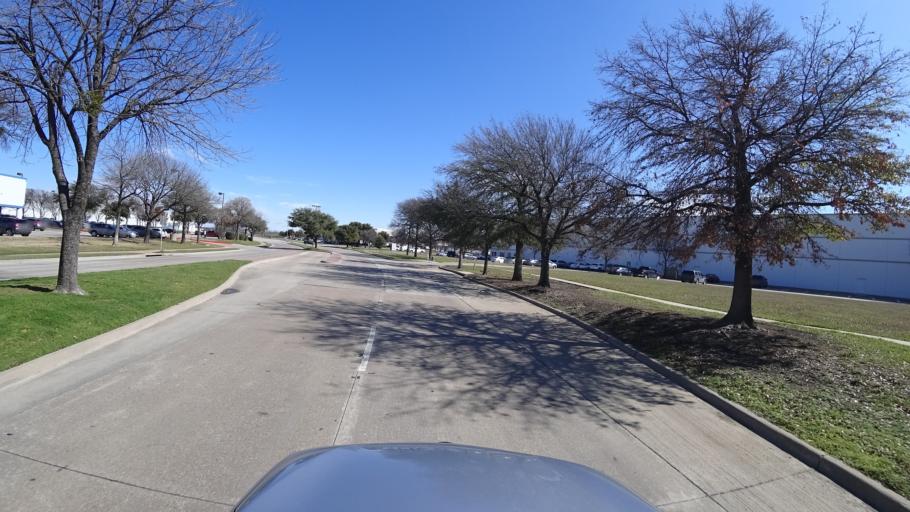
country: US
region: Texas
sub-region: Denton County
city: Lewisville
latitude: 33.0210
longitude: -96.9749
